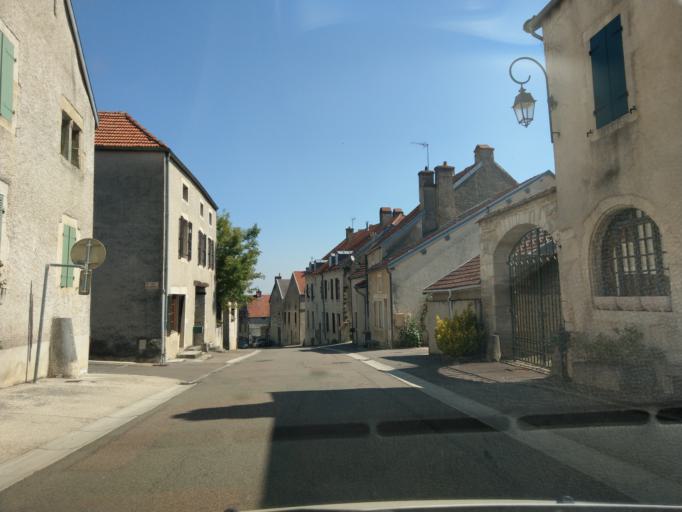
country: FR
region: Bourgogne
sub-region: Departement de la Cote-d'Or
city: Marcilly-sur-Tille
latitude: 47.5163
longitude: 5.1761
